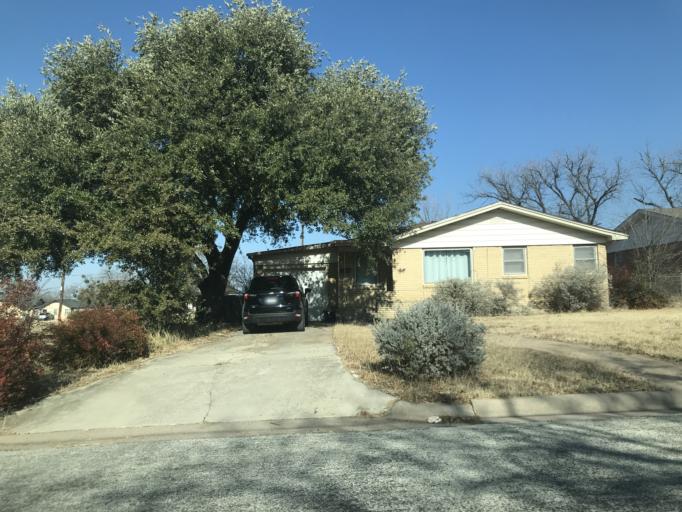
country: US
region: Texas
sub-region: Taylor County
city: Abilene
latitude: 32.4686
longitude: -99.7154
